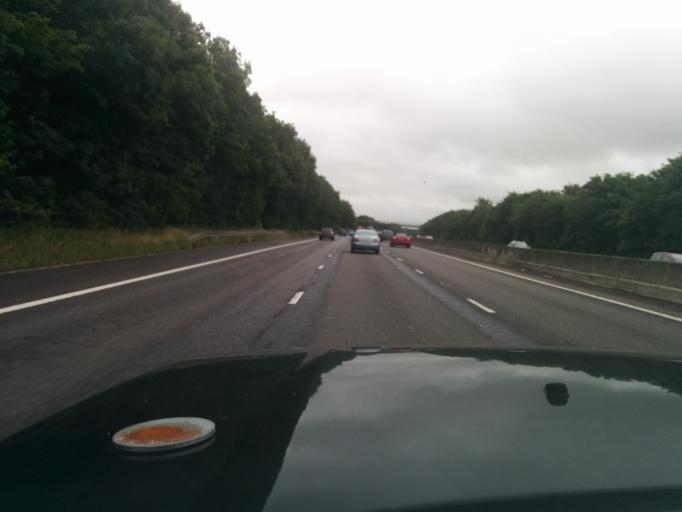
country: GB
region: England
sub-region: West Berkshire
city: Lambourn
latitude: 51.4837
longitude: -1.5607
